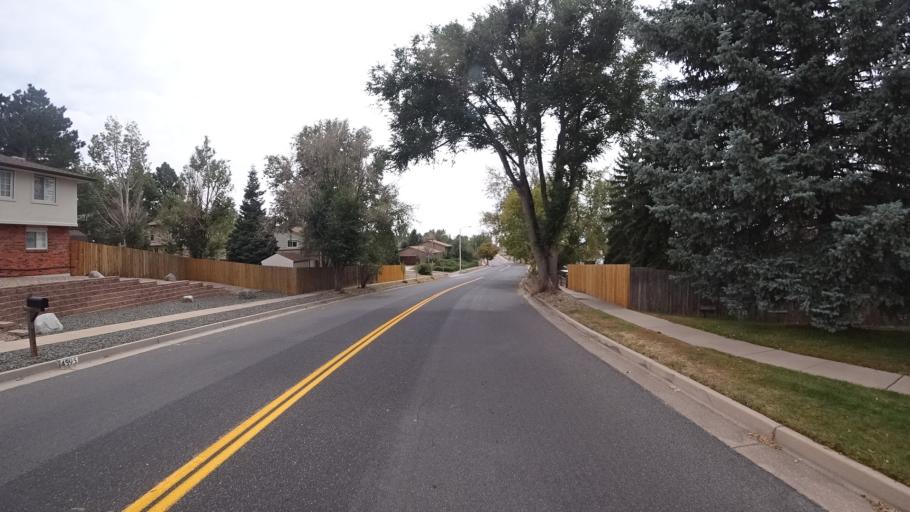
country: US
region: Colorado
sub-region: El Paso County
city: Cimarron Hills
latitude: 38.8979
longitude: -104.7329
